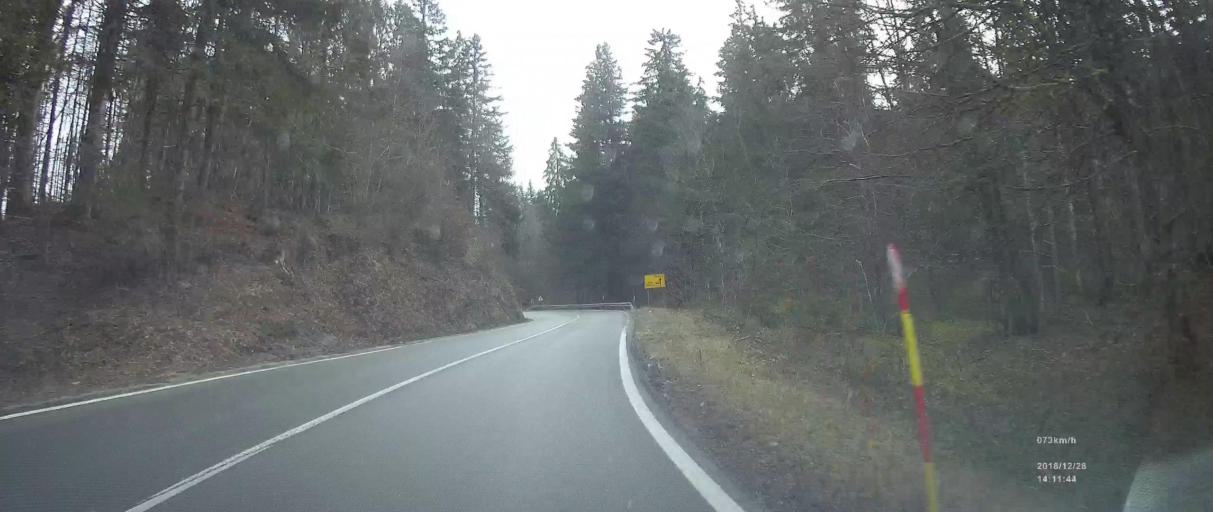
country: SI
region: Kostel
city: Kostel
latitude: 45.4475
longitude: 14.9901
